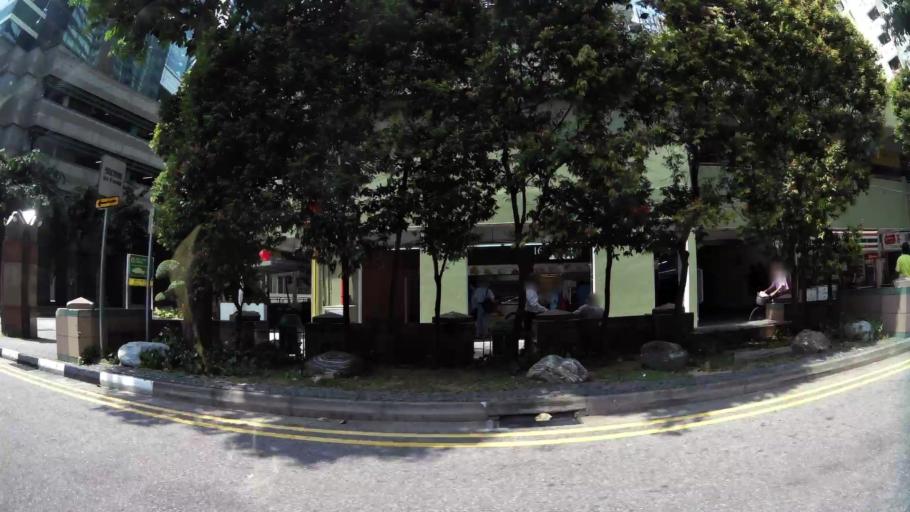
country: SG
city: Singapore
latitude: 1.2747
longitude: 103.8429
